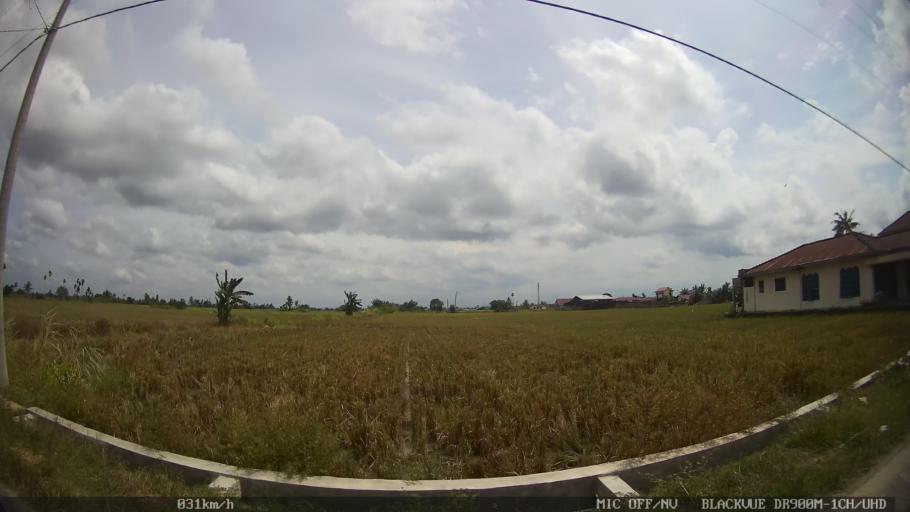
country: ID
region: North Sumatra
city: Percut
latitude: 3.5726
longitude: 98.8429
